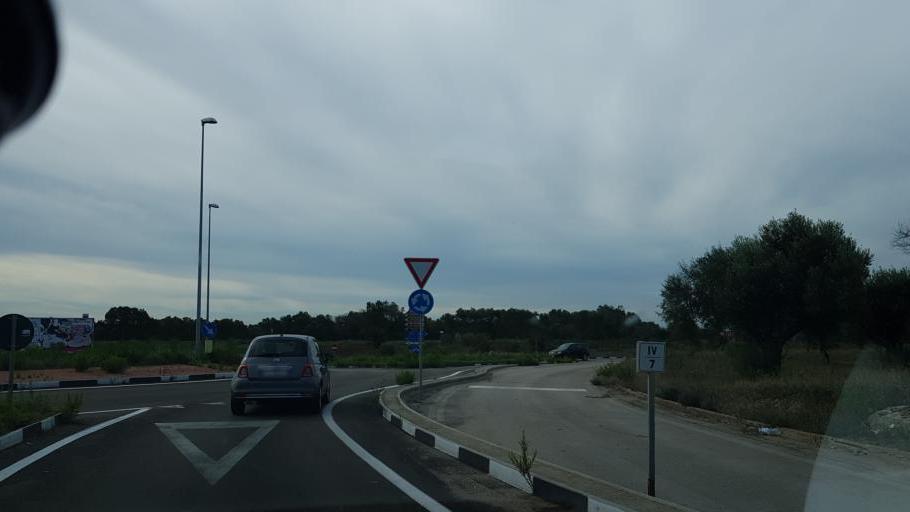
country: IT
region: Apulia
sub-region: Provincia di Lecce
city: Vernole
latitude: 40.3293
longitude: 18.3367
